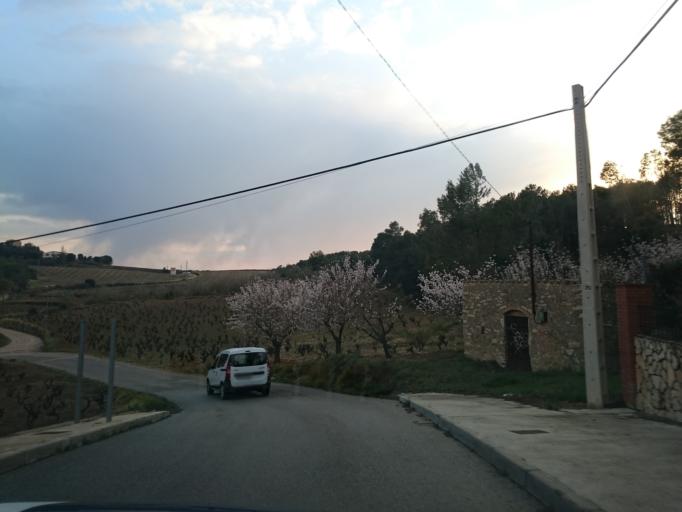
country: ES
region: Catalonia
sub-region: Provincia de Barcelona
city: Sant Marti Sarroca
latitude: 41.4168
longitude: 1.5464
